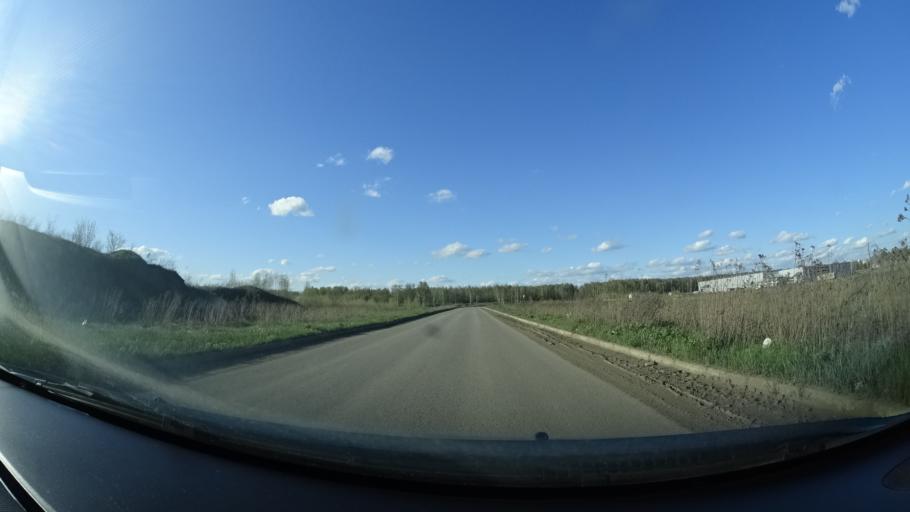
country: RU
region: Bashkortostan
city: Ufa
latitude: 54.6777
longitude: 55.9254
